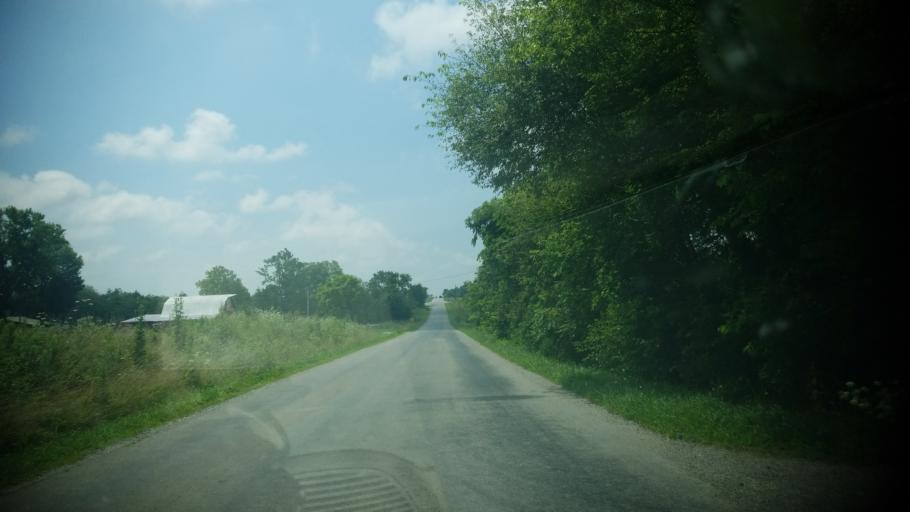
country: US
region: Illinois
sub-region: Wayne County
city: Fairfield
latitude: 38.5155
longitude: -88.3485
